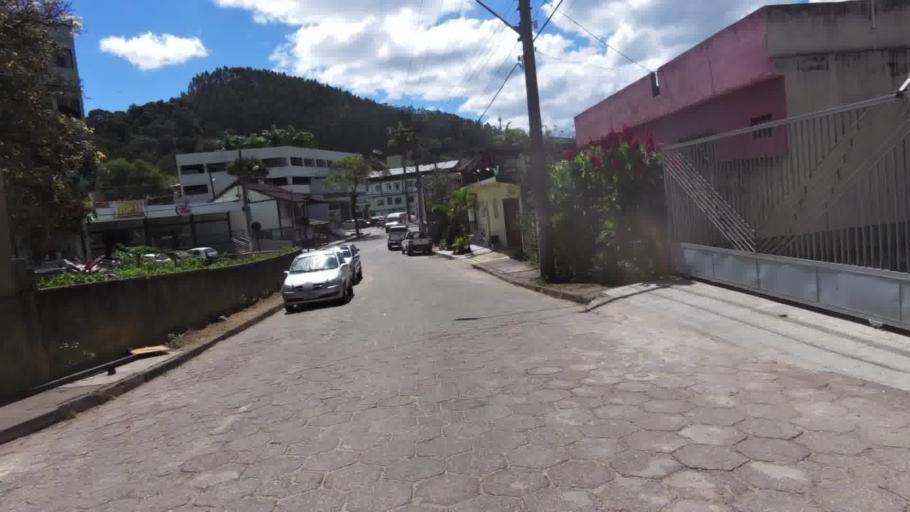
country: BR
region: Espirito Santo
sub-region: Vargem Alta
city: Vargem Alta
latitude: -20.6748
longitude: -41.0117
